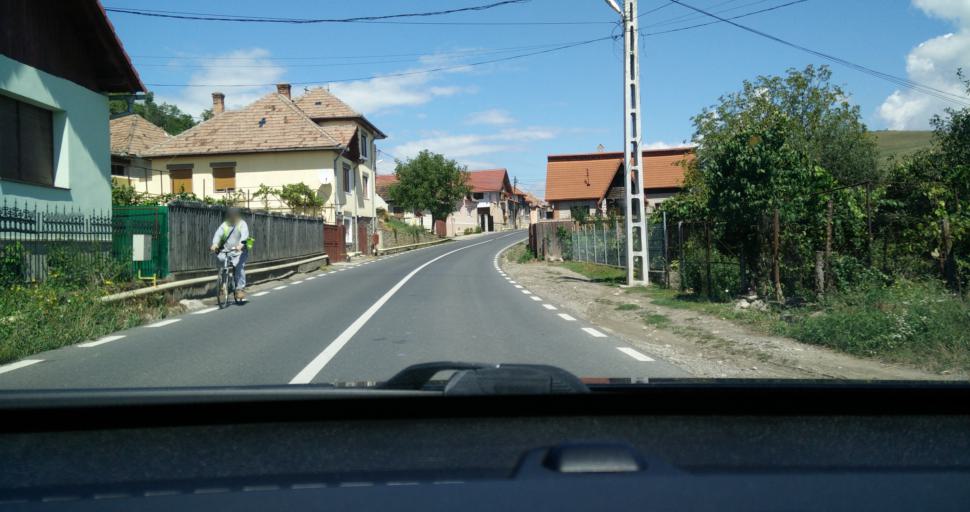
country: RO
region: Alba
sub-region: Comuna Sasciori
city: Sebesel
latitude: 45.8837
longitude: 23.5657
